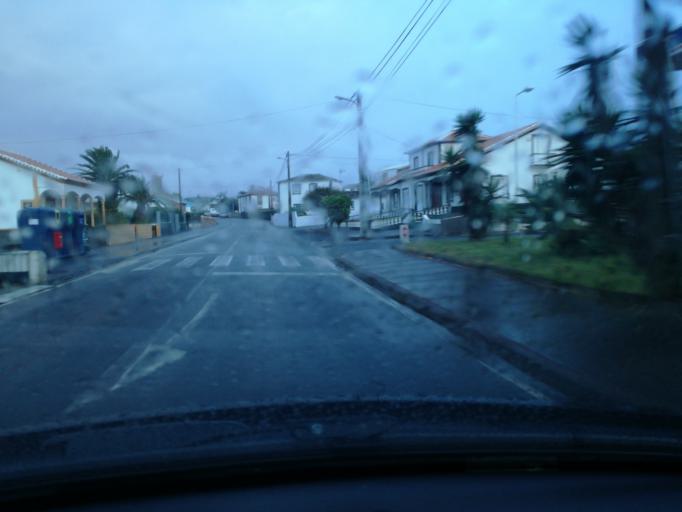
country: PT
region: Azores
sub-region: Praia da Vitoria
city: Praia da Vitoria
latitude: 38.7099
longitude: -27.0609
